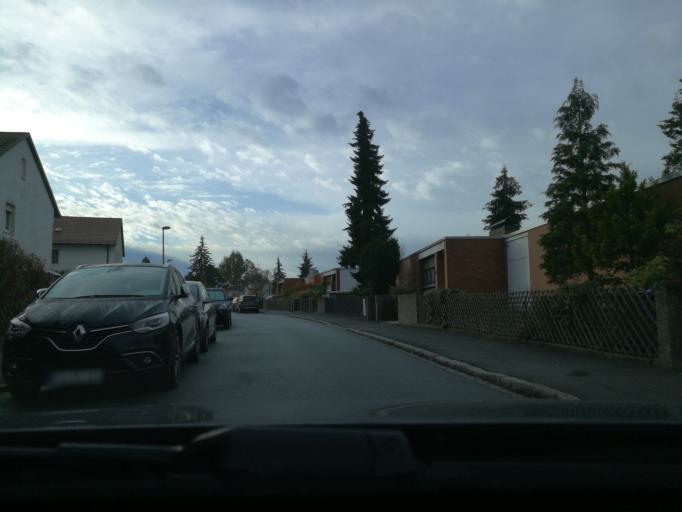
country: DE
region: Bavaria
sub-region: Regierungsbezirk Mittelfranken
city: Furth
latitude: 49.4811
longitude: 10.9506
